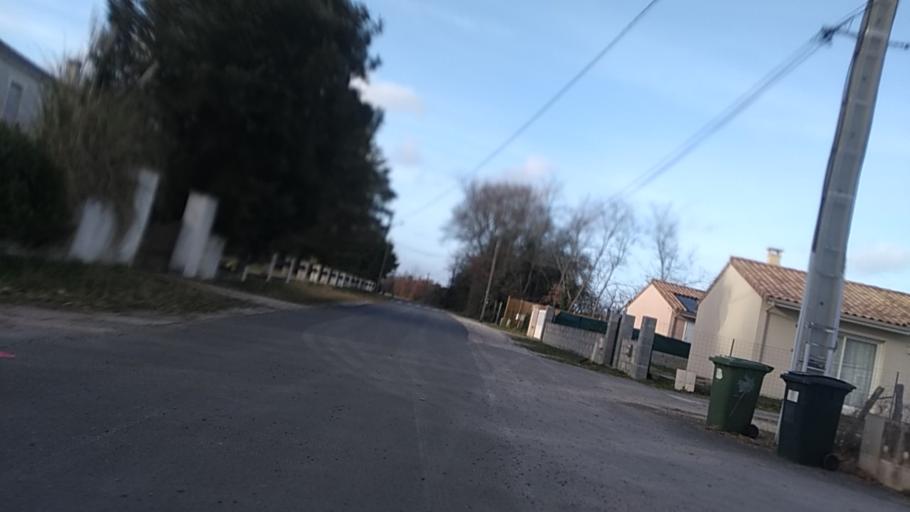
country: FR
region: Aquitaine
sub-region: Departement de la Gironde
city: Le Barp
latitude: 44.5962
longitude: -0.7681
